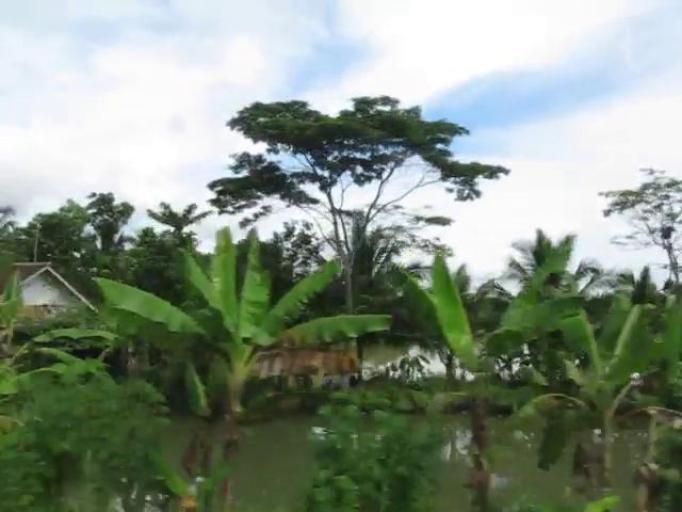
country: ID
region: Central Java
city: Meluwung
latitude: -7.3937
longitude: 108.6991
